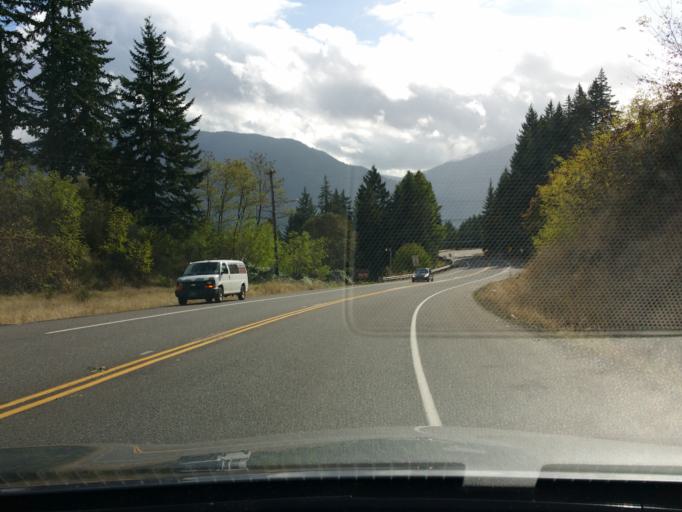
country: US
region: Washington
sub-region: Skamania County
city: Carson
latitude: 45.7227
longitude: -121.8202
